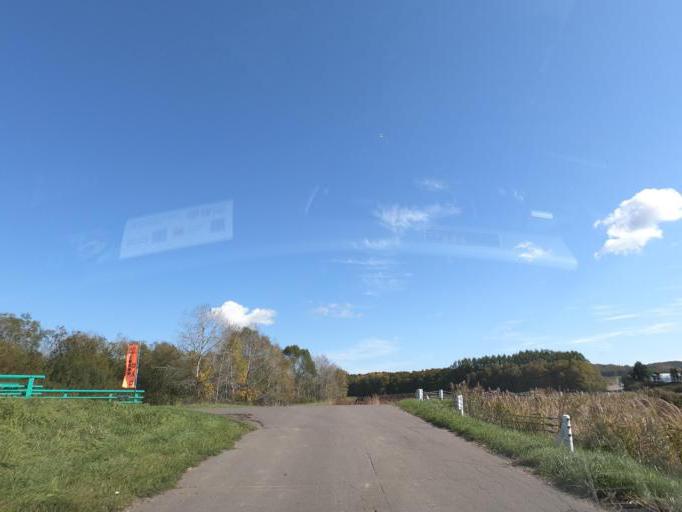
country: JP
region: Hokkaido
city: Otofuke
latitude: 43.0591
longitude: 143.2793
